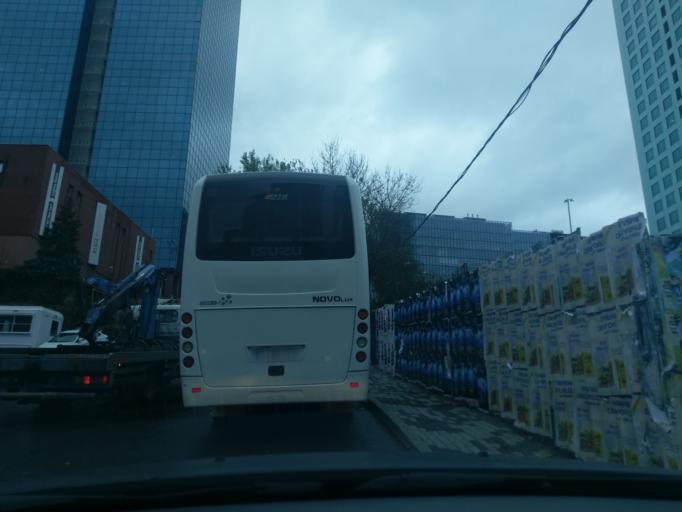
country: TR
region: Istanbul
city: Sisli
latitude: 41.1107
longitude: 29.0203
